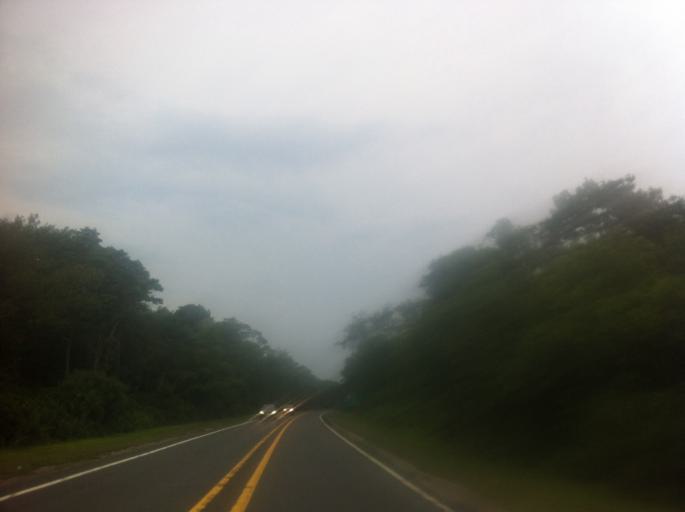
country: US
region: New York
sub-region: Nassau County
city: North Massapequa
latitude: 40.7152
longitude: -73.4580
